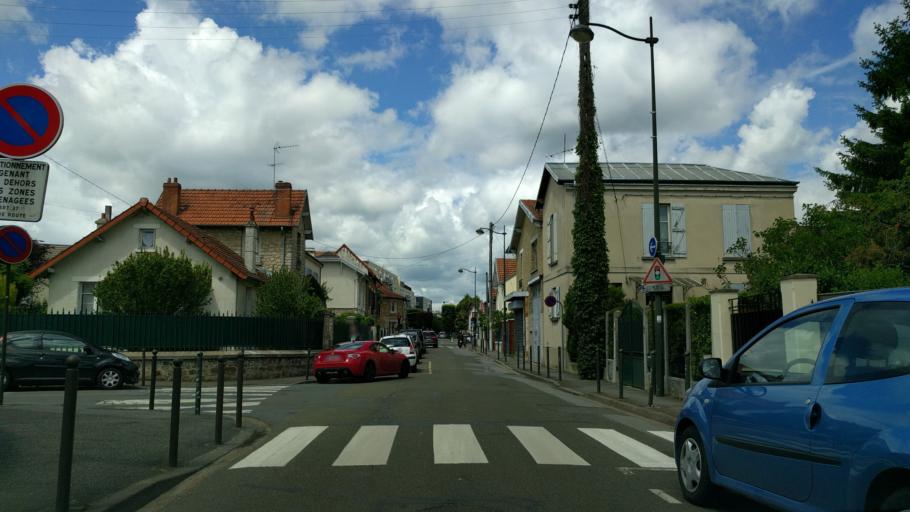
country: FR
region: Ile-de-France
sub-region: Departement des Yvelines
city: Le Chesnay
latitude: 48.8216
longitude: 2.1337
